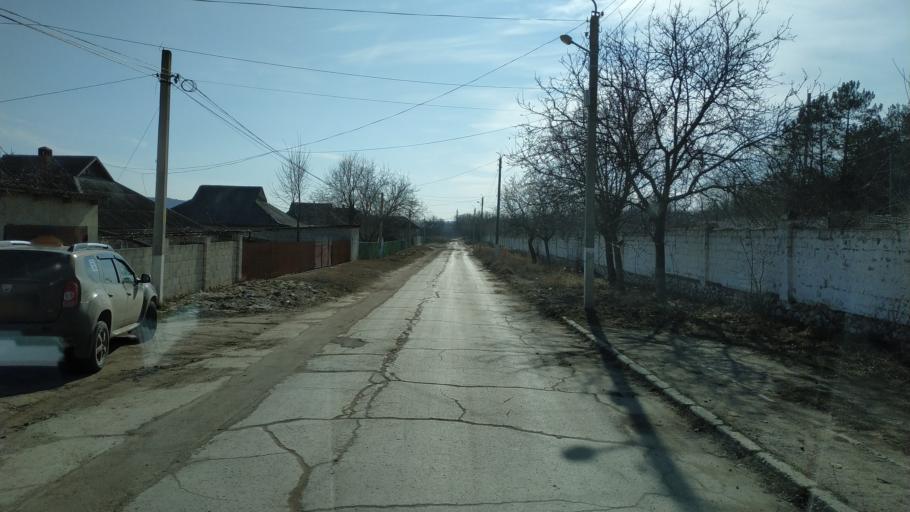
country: MD
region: Nisporeni
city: Nisporeni
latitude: 47.0661
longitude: 28.1731
